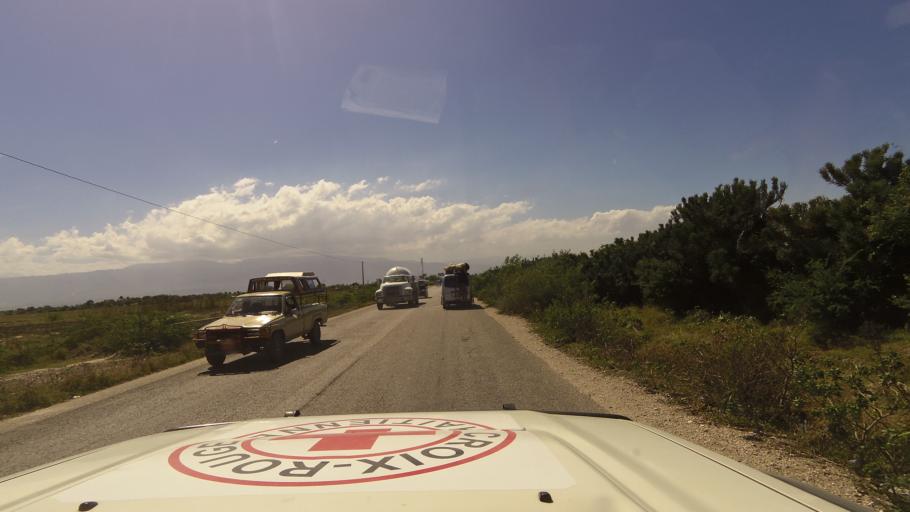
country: HT
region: Ouest
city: Delmas 73
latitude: 18.6416
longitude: -72.3012
